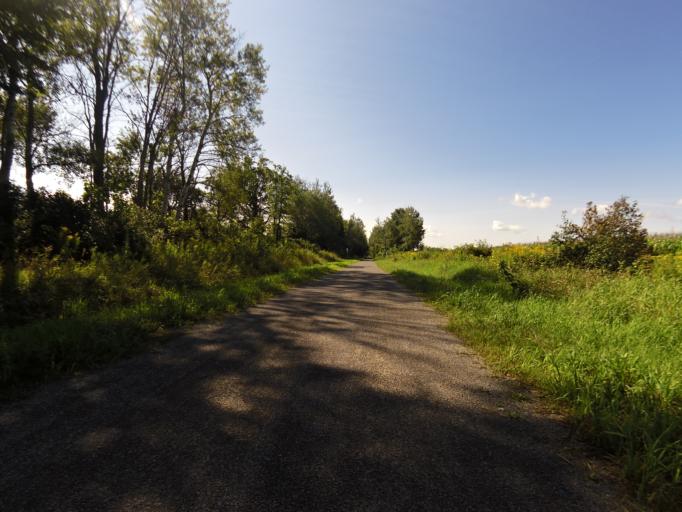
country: CA
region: Ontario
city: Bells Corners
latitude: 45.1527
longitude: -75.6133
